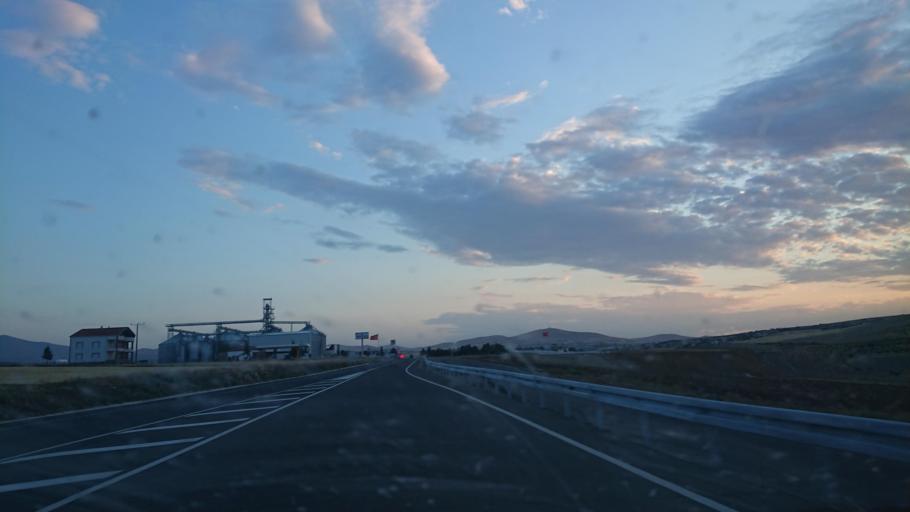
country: TR
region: Aksaray
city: Balci
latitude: 38.7673
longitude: 34.0960
